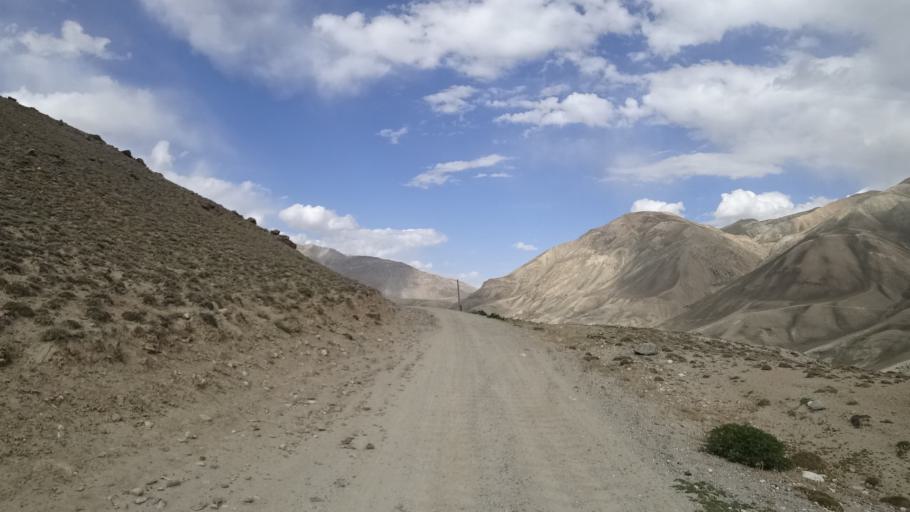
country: AF
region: Badakhshan
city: Khandud
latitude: 37.1966
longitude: 72.7704
